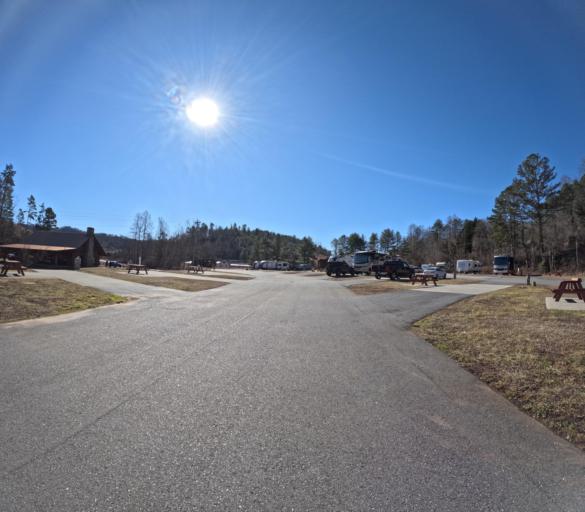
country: US
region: North Carolina
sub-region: Cherokee County
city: Murphy
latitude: 35.1233
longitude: -84.0013
